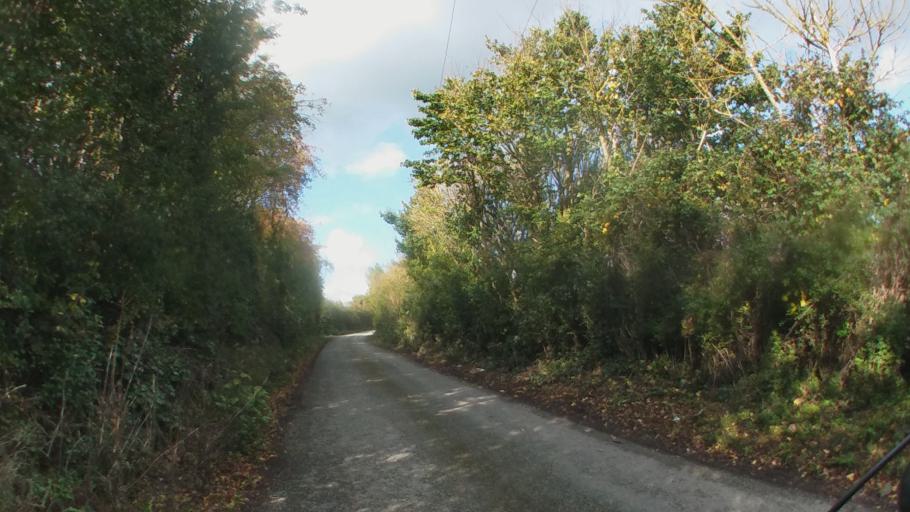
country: IE
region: Leinster
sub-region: Kilkenny
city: Kilkenny
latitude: 52.6732
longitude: -7.2373
